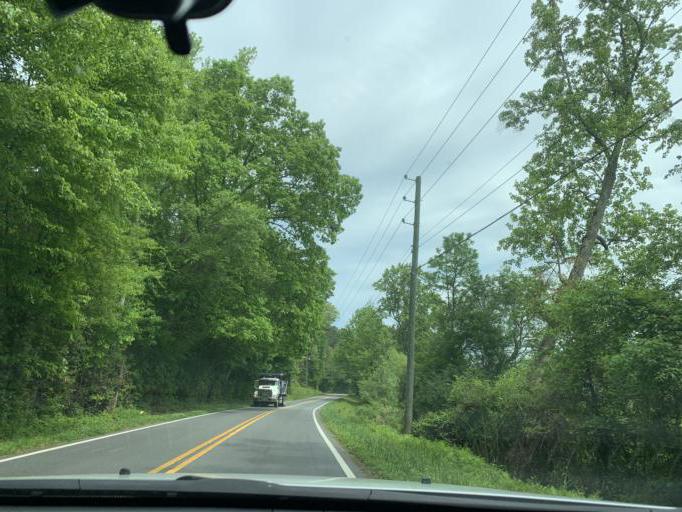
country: US
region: Georgia
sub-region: Forsyth County
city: Cumming
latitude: 34.1514
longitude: -84.1972
